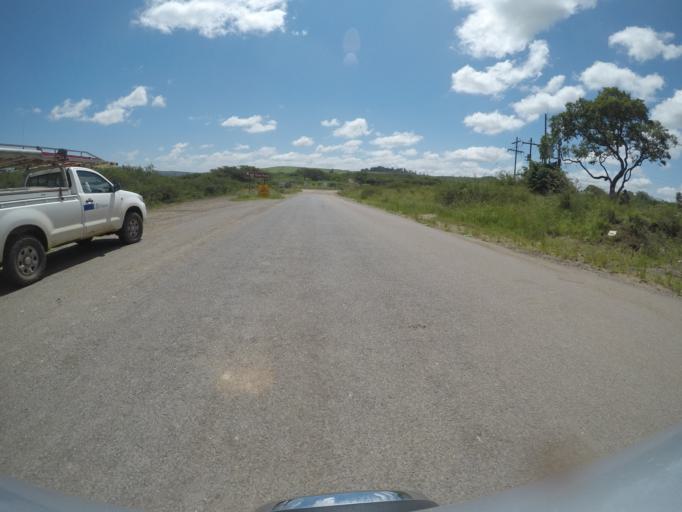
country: ZA
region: KwaZulu-Natal
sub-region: uThungulu District Municipality
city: Empangeni
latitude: -28.6624
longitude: 31.7851
